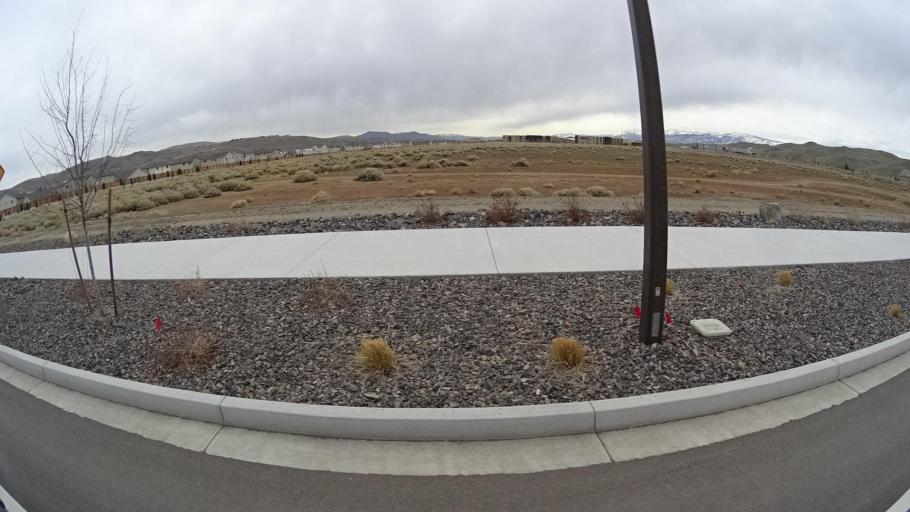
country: US
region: Nevada
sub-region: Washoe County
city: Spanish Springs
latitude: 39.6153
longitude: -119.7200
